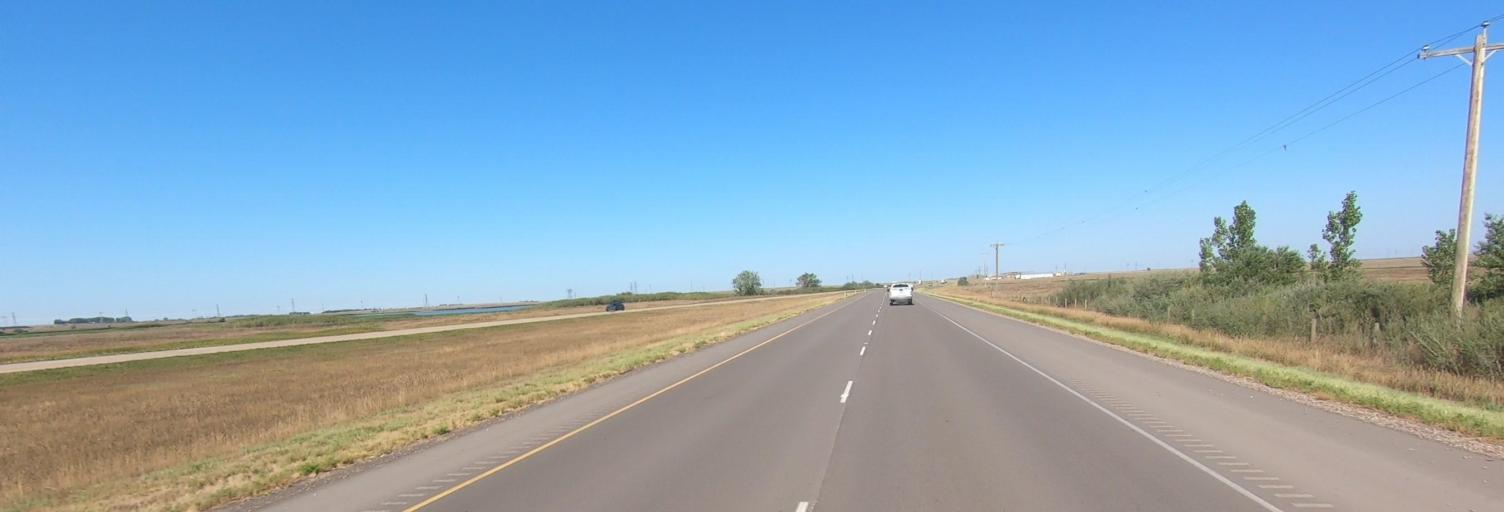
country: CA
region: Alberta
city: Brooks
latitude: 50.6190
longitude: -111.9483
